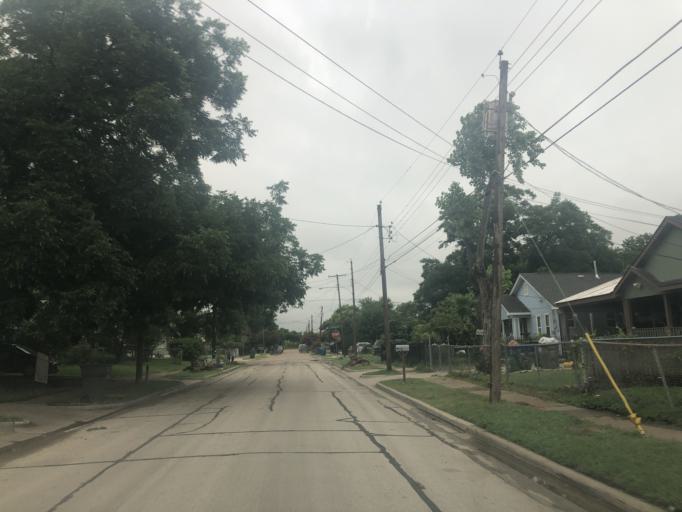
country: US
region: Texas
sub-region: Dallas County
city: Cockrell Hill
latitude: 32.7846
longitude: -96.8800
